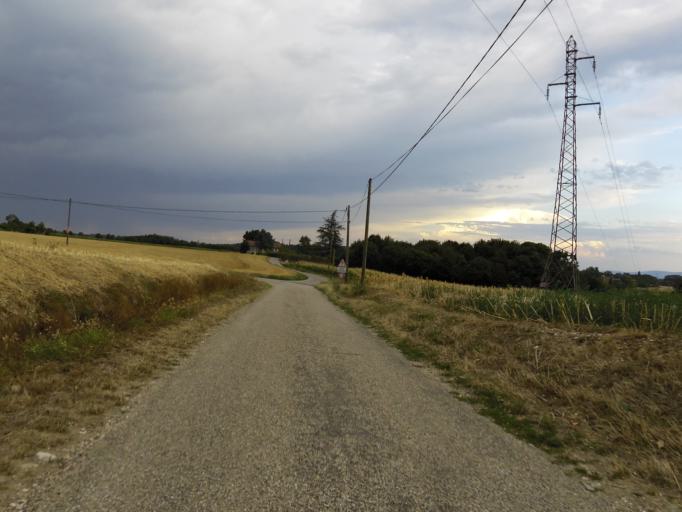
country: FR
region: Rhone-Alpes
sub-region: Departement de l'Ain
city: Perouges
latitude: 45.9154
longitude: 5.1711
